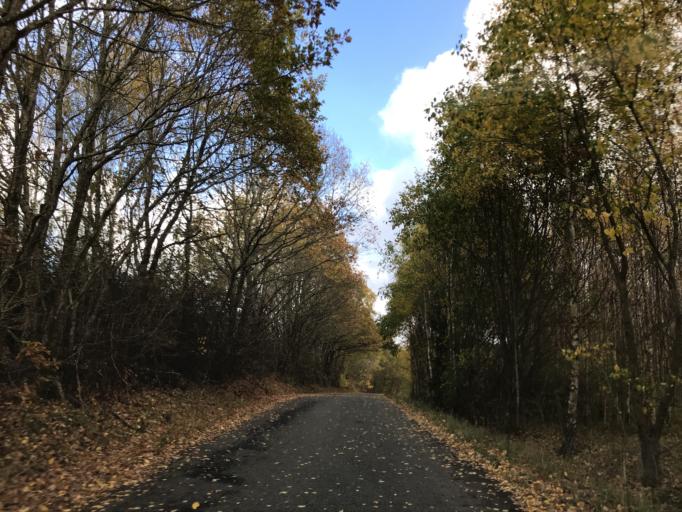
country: SE
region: Skane
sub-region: Perstorps Kommun
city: Perstorp
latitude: 56.0305
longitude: 13.3920
